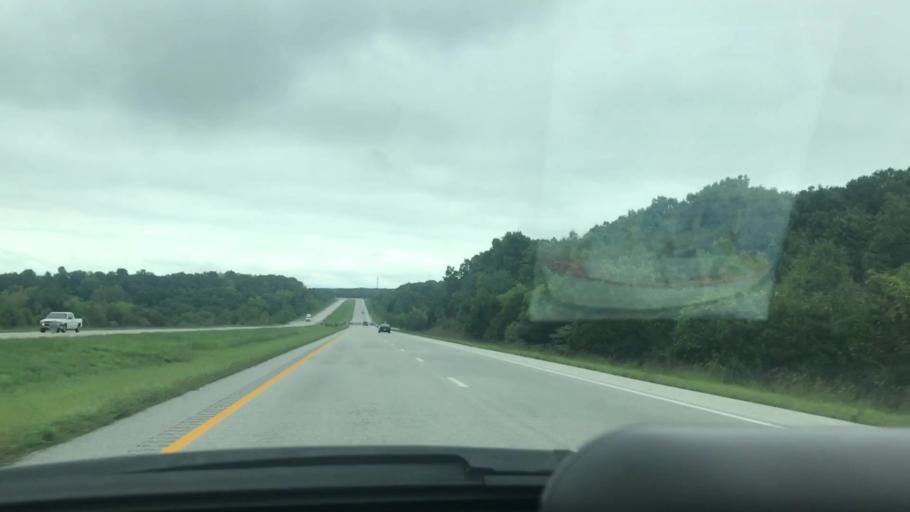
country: US
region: Missouri
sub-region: Greene County
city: Strafford
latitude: 37.3064
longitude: -93.1744
